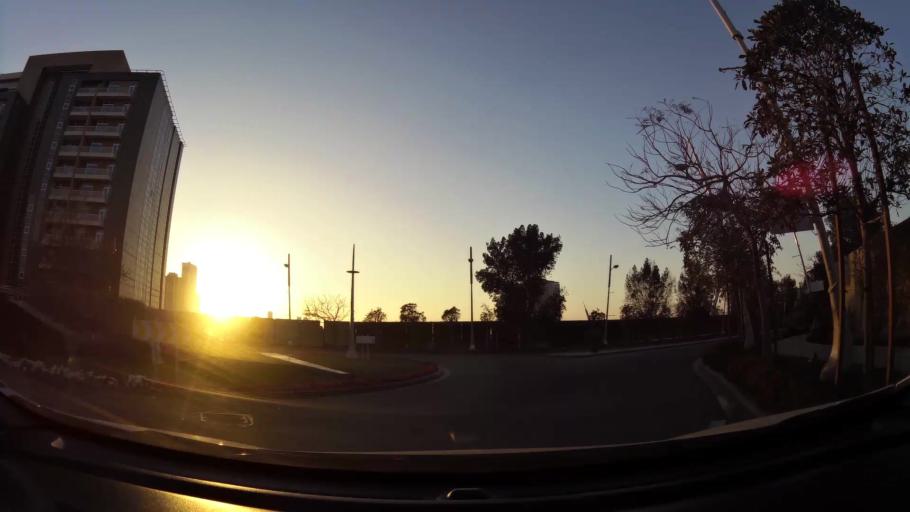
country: BH
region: Manama
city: Jidd Hafs
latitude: 26.2390
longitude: 50.5630
